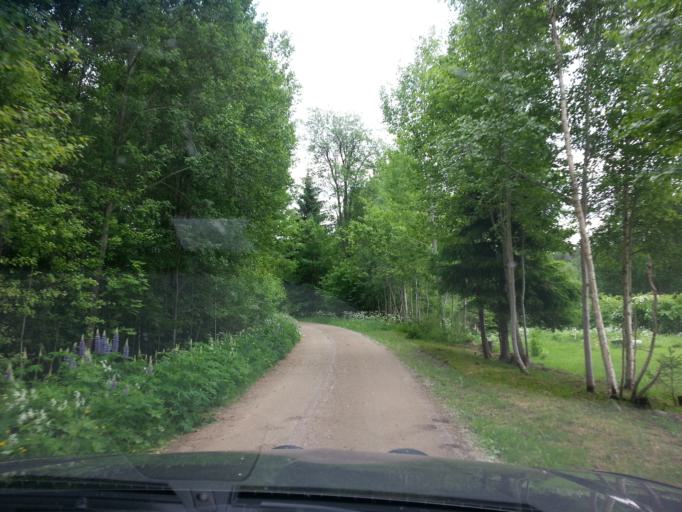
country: SE
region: Joenkoeping
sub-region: Vetlanda Kommun
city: Vetlanda
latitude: 57.2858
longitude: 15.1283
